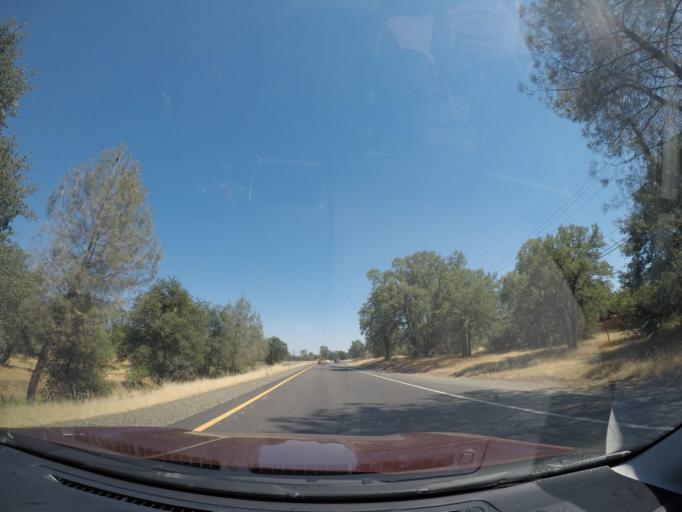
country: US
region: California
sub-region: Shasta County
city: Redding
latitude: 40.6103
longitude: -122.3642
